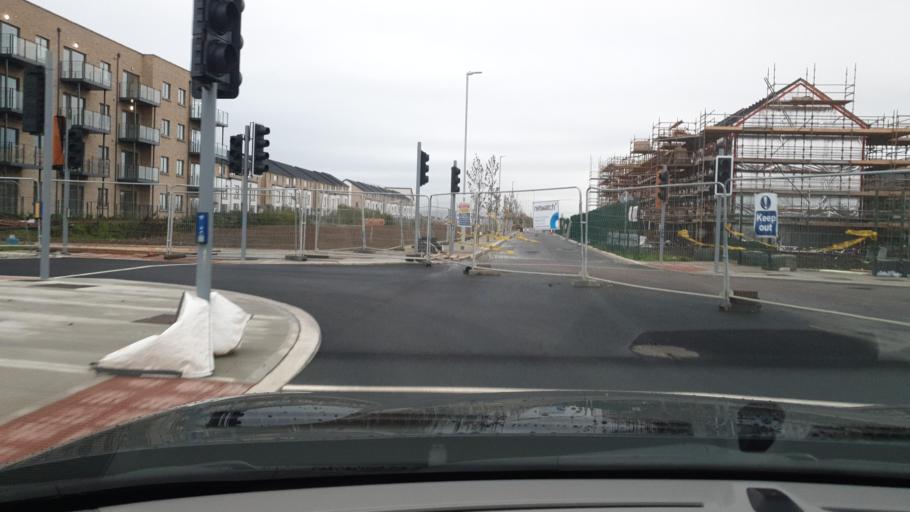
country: IE
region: Leinster
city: Lucan
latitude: 53.3429
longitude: -6.4737
